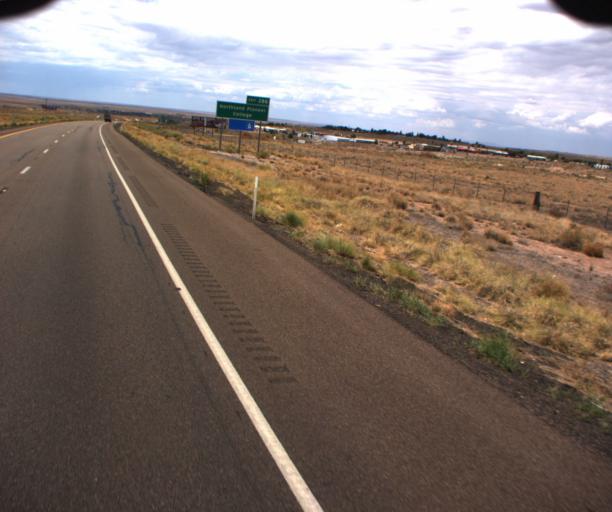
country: US
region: Arizona
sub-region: Navajo County
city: Holbrook
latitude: 34.9200
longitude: -110.1416
